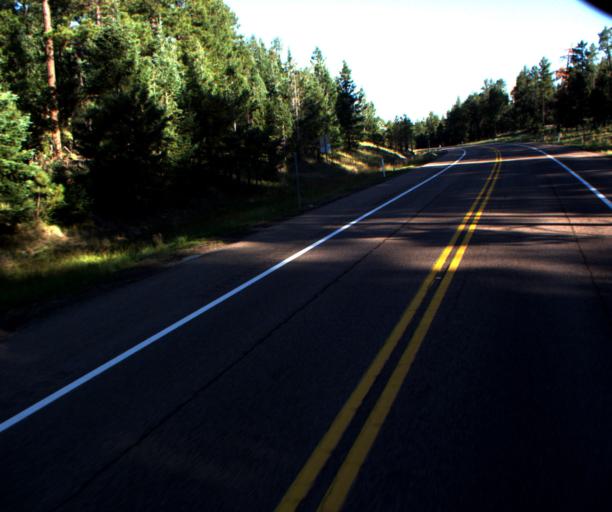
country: US
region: Arizona
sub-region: Apache County
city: Eagar
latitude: 33.8963
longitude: -109.1551
